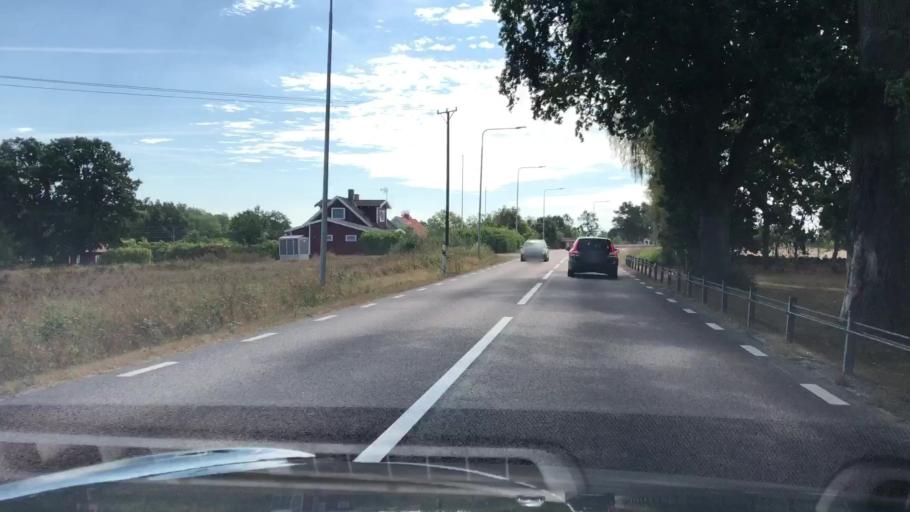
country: SE
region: Kalmar
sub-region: Torsas Kommun
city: Torsas
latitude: 56.3807
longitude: 16.0696
